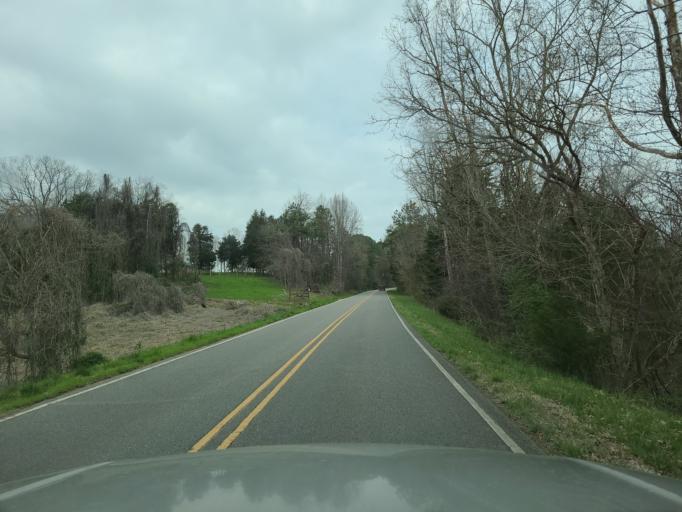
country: US
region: North Carolina
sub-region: Cleveland County
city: Shelby
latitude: 35.3339
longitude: -81.5355
